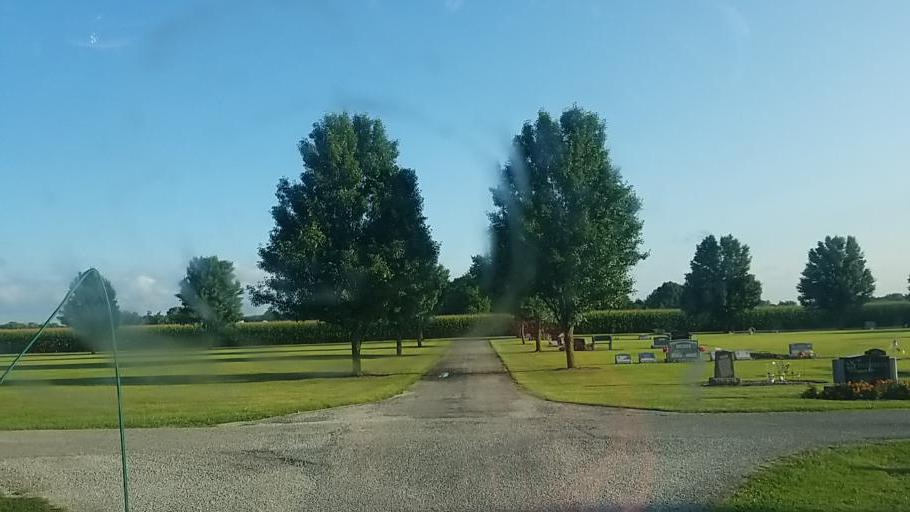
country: US
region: Ohio
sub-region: Crawford County
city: Galion
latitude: 40.6680
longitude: -82.8343
